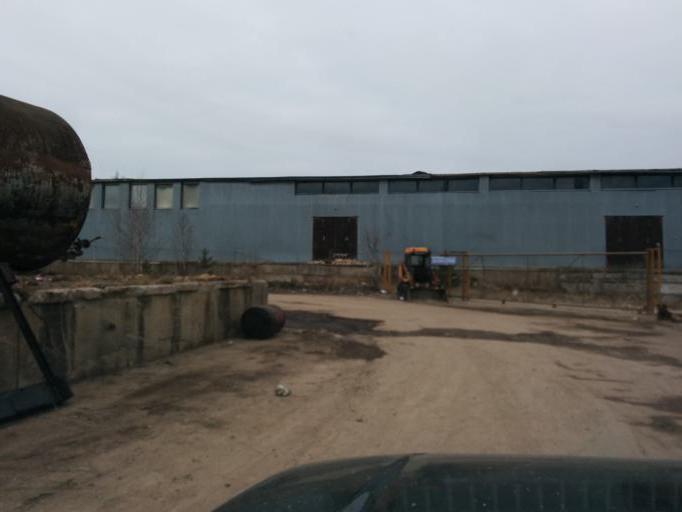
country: LV
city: Tireli
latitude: 56.9450
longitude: 23.6347
